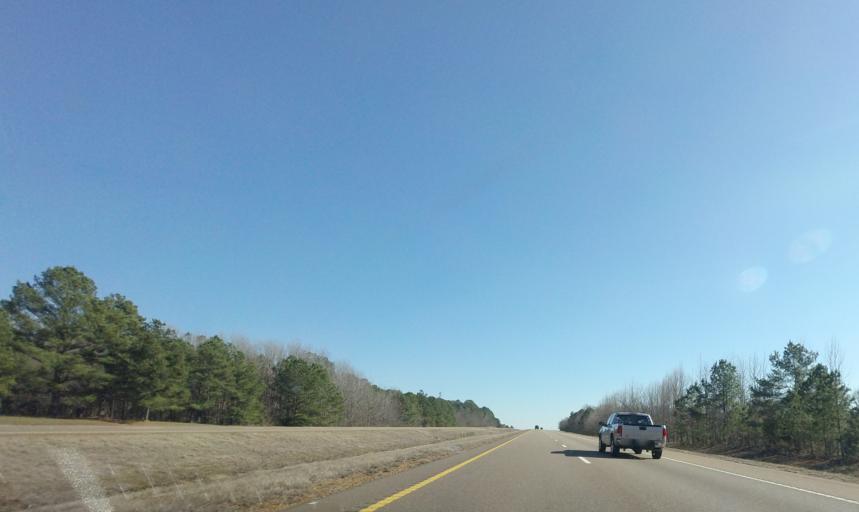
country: US
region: Mississippi
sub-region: Marshall County
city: Holly Springs
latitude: 34.8165
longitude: -89.5360
